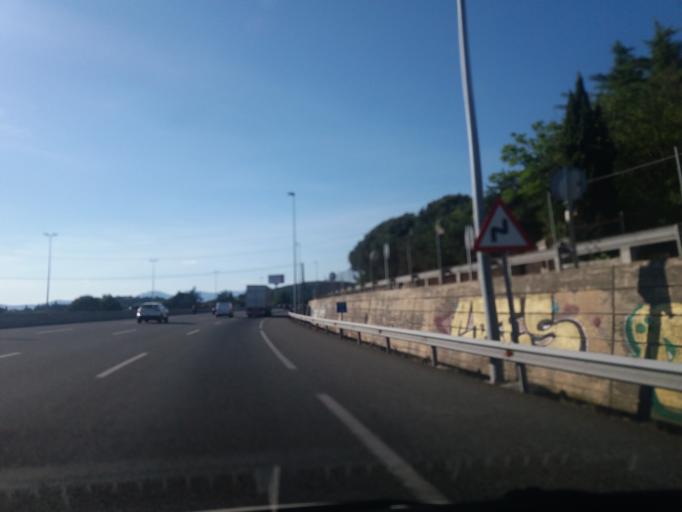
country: ES
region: Madrid
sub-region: Provincia de Madrid
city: Torrelodones
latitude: 40.5866
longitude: -3.9530
